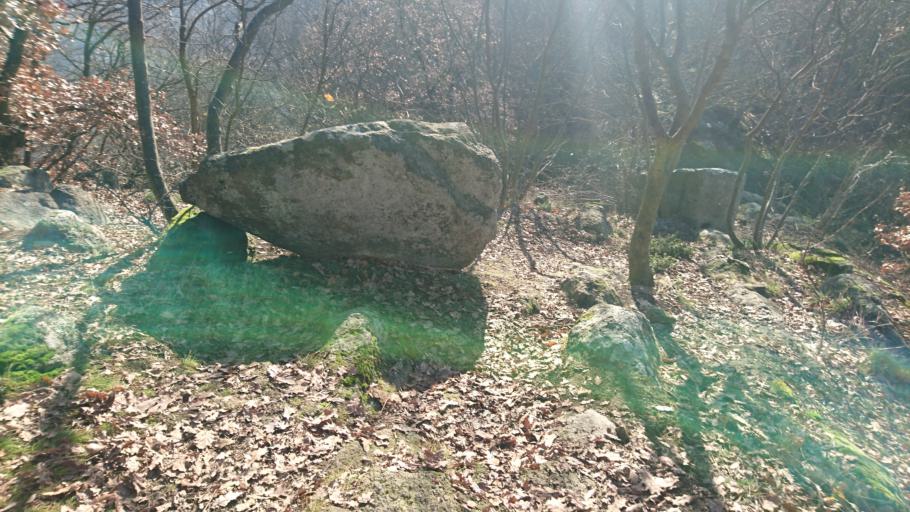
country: IT
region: Veneto
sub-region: Provincia di Padova
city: Treponti
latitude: 45.3348
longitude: 11.6846
